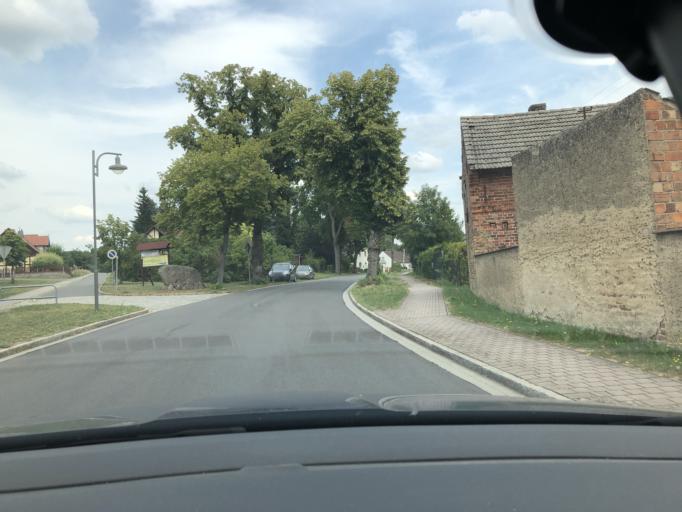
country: DE
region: Brandenburg
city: Schlepzig
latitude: 52.0333
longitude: 13.8361
